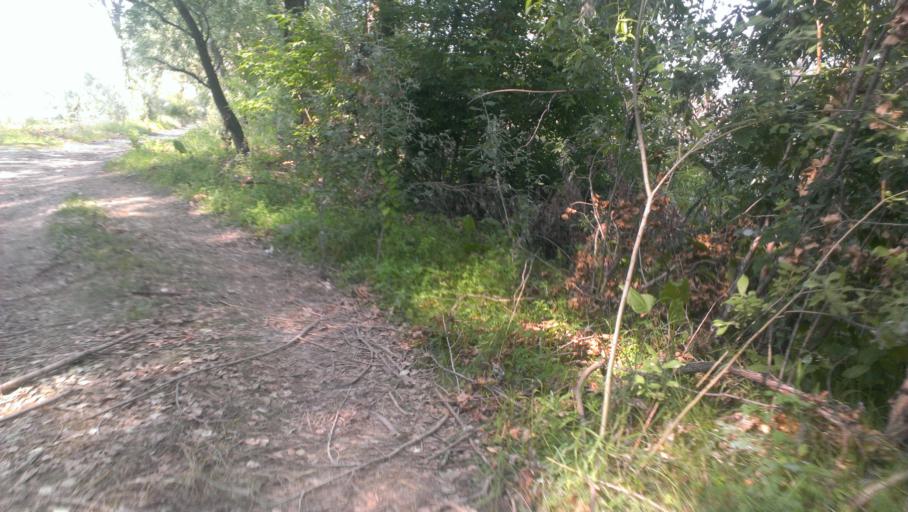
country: RU
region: Altai Krai
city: Novoaltaysk
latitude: 53.3729
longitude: 83.8569
